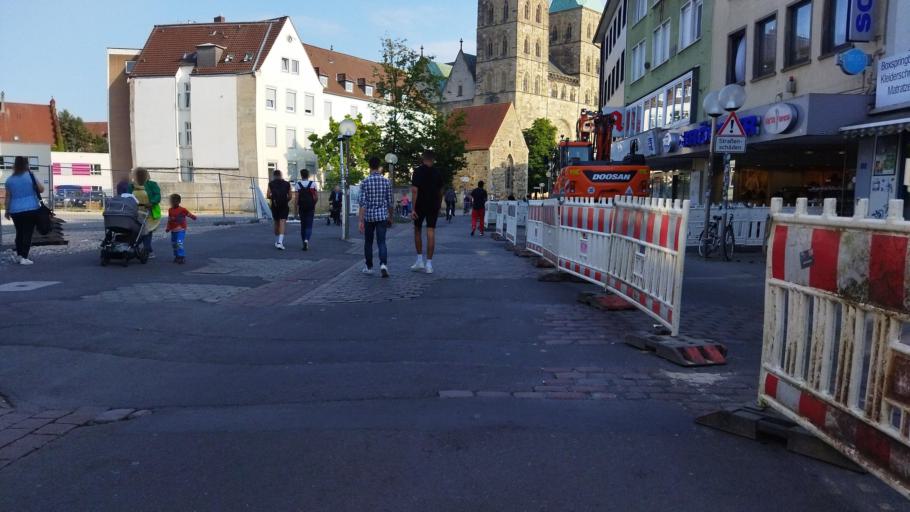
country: DE
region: Lower Saxony
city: Osnabrueck
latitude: 52.2714
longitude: 8.0497
